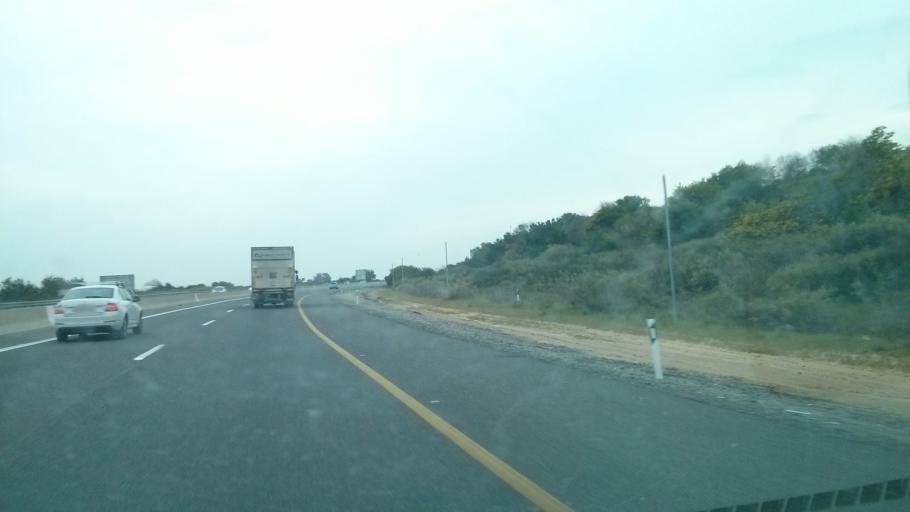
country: IL
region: Haifa
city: Qesarya
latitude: 32.4931
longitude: 34.9181
